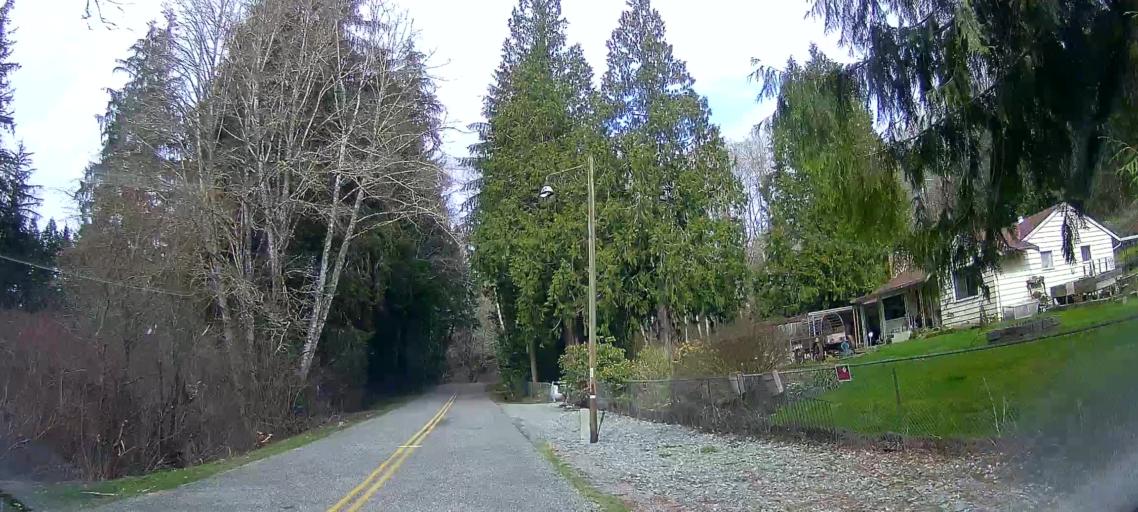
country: US
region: Washington
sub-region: Skagit County
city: Burlington
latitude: 48.5900
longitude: -122.3278
